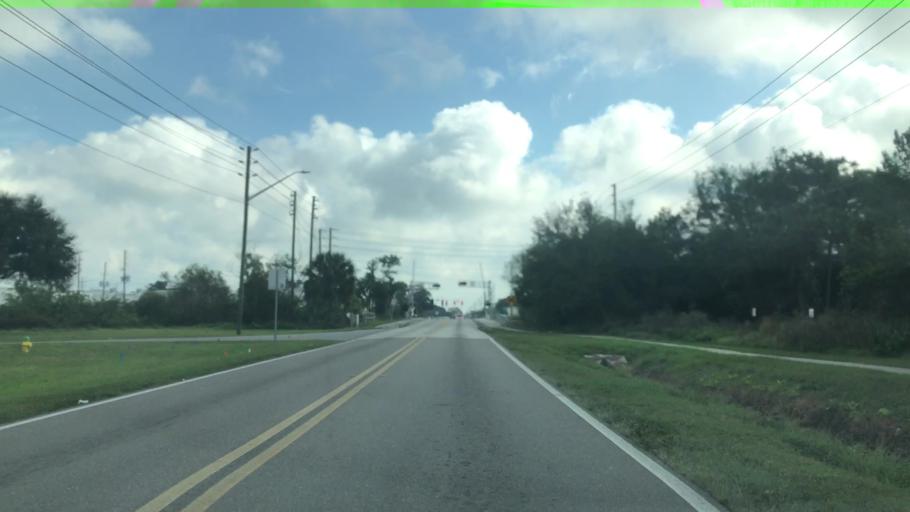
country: US
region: Florida
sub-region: Pinellas County
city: Pinellas Park
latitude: 27.8283
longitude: -82.7024
